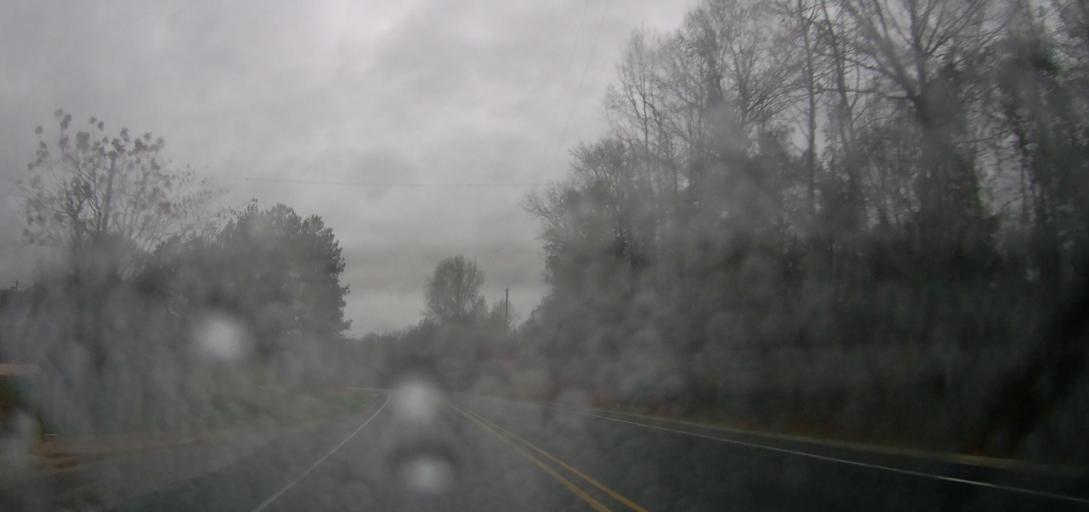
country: US
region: Alabama
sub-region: Chilton County
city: Clanton
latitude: 32.6213
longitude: -86.7363
